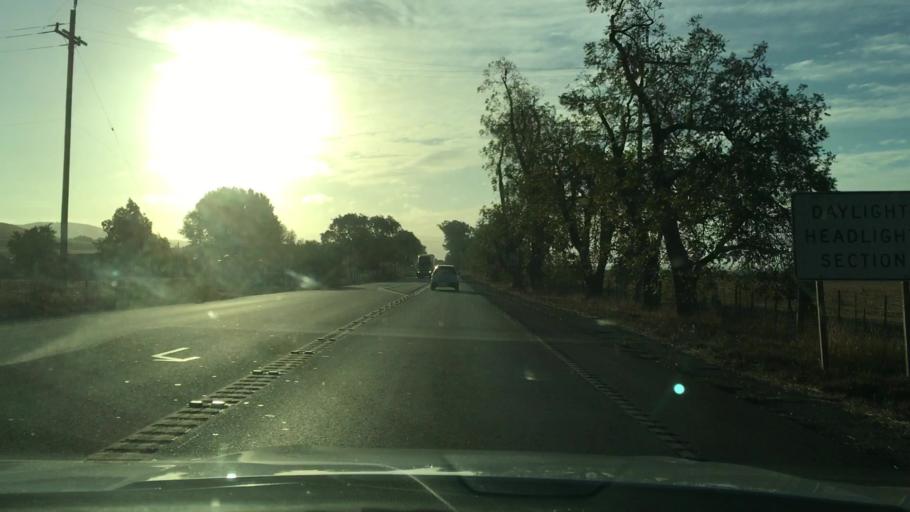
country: US
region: California
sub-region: Santa Clara County
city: Gilroy
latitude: 36.9882
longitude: -121.4900
